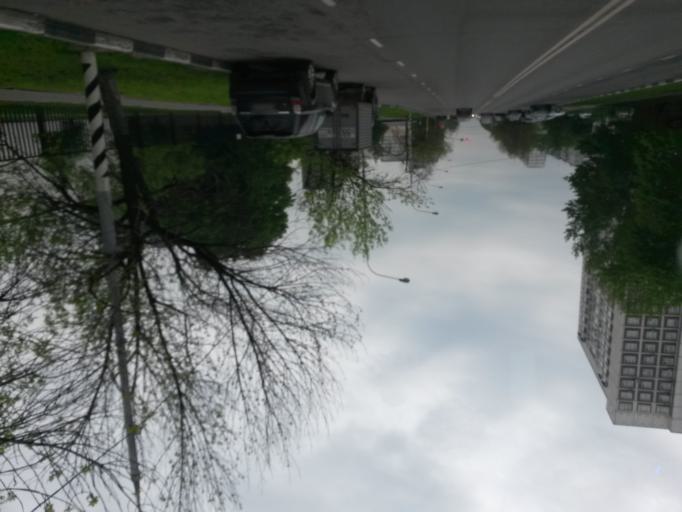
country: RU
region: Moscow
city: Orekhovo-Borisovo
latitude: 55.6219
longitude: 37.7167
